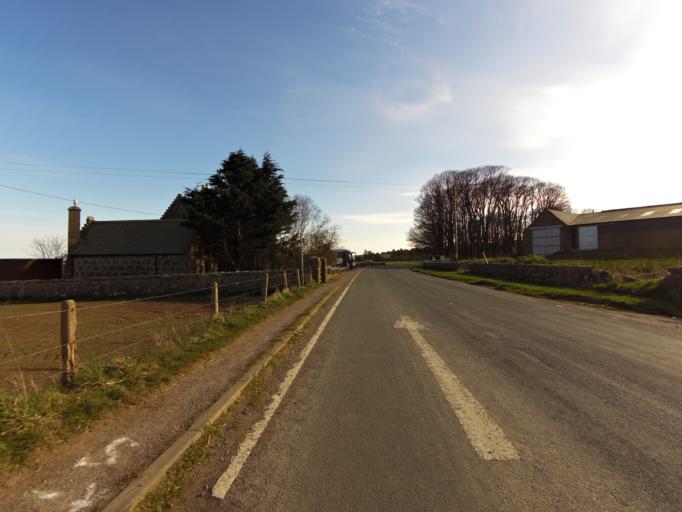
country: GB
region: Scotland
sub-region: Aberdeenshire
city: Stonehaven
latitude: 56.9460
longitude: -2.2058
